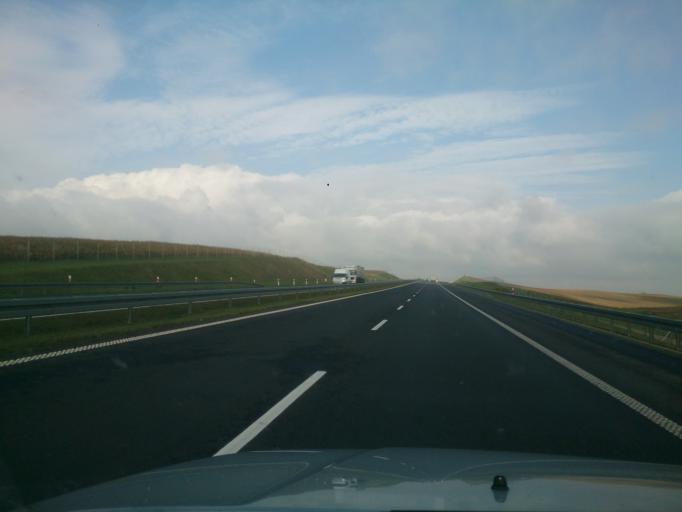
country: PL
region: Pomeranian Voivodeship
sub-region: Powiat starogardzki
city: Bobowo
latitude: 53.8394
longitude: 18.6275
